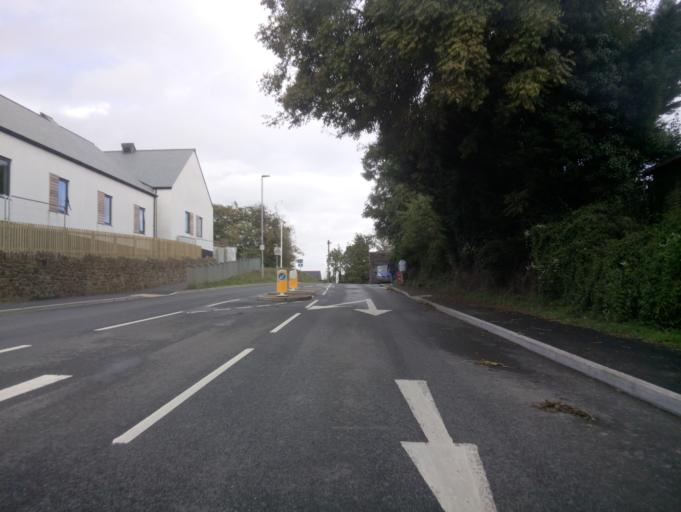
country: GB
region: England
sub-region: Devon
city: Modbury
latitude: 50.3501
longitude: -3.8910
